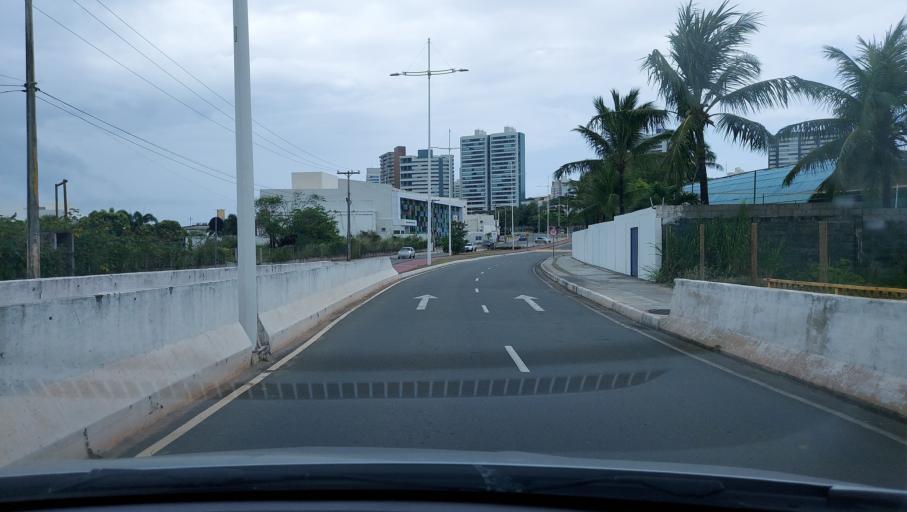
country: BR
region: Bahia
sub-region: Lauro De Freitas
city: Lauro de Freitas
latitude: -12.9565
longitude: -38.3996
